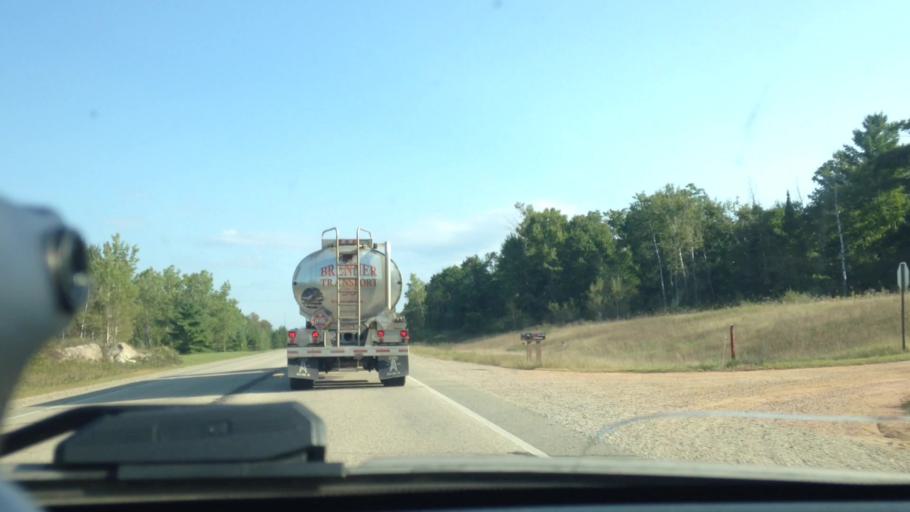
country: US
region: Wisconsin
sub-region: Marinette County
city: Niagara
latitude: 45.6536
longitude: -87.9630
